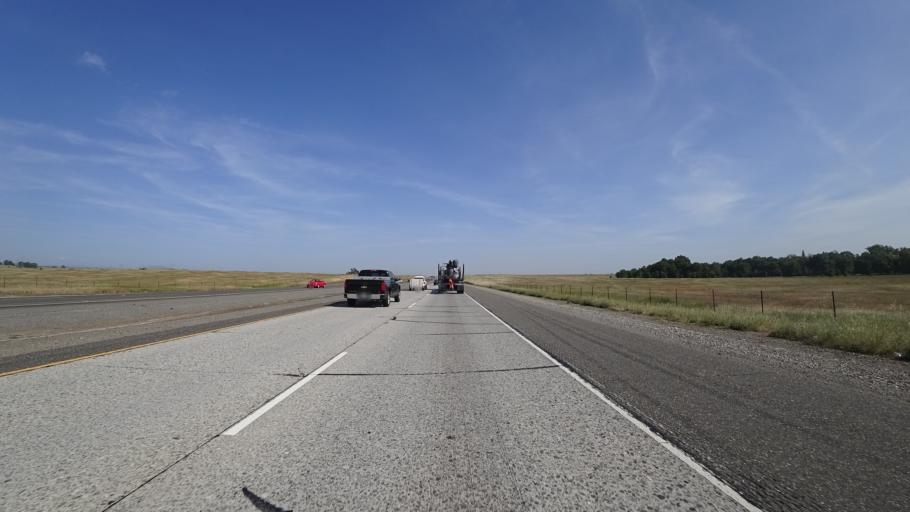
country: US
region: California
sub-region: Butte County
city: Durham
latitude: 39.6821
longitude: -121.7646
